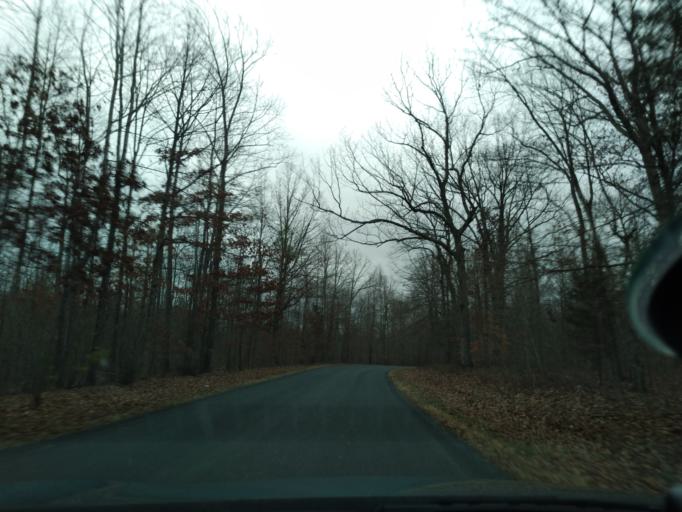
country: US
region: Virginia
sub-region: Appomattox County
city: Appomattox
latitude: 37.4062
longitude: -78.6672
